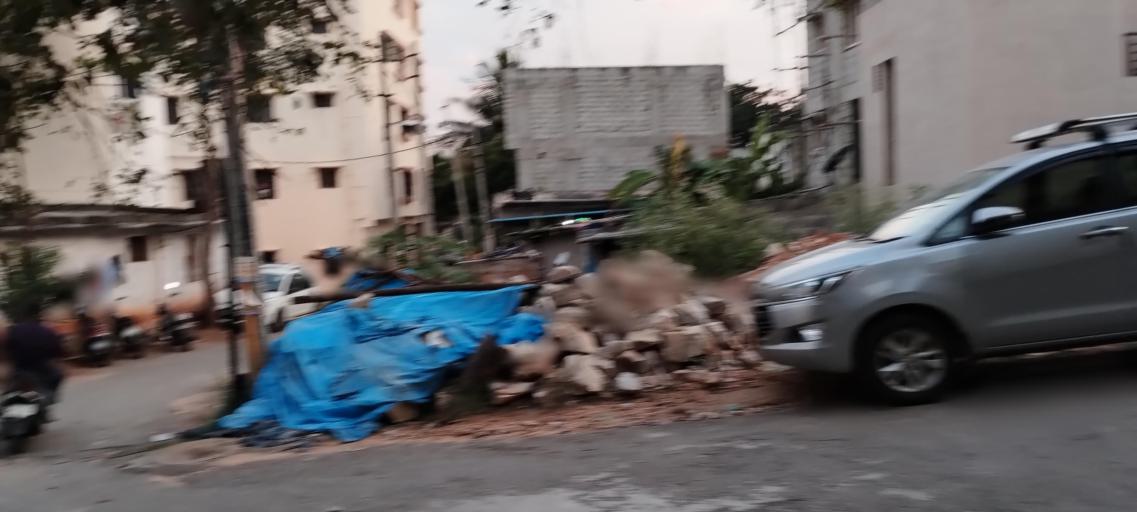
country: IN
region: Karnataka
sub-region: Bangalore Urban
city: Bangalore
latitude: 12.9371
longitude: 77.5389
